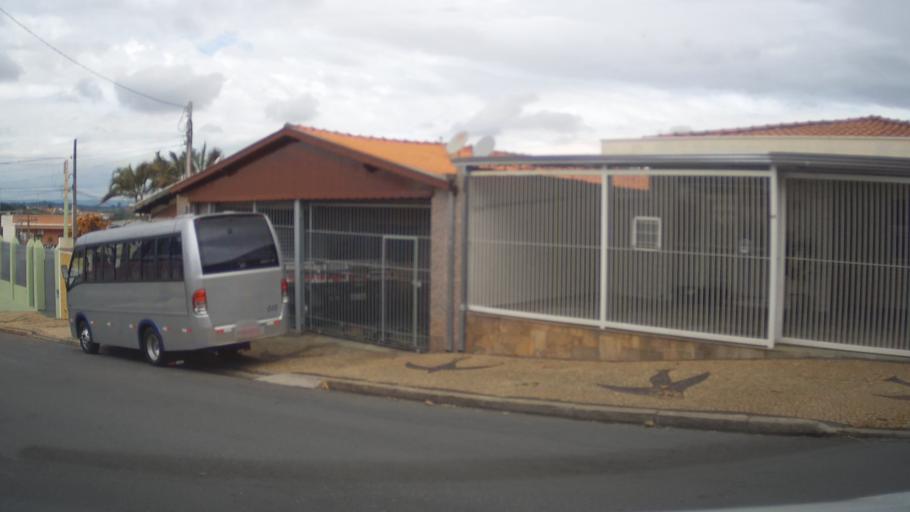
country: BR
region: Sao Paulo
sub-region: Campinas
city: Campinas
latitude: -22.9338
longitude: -47.0315
